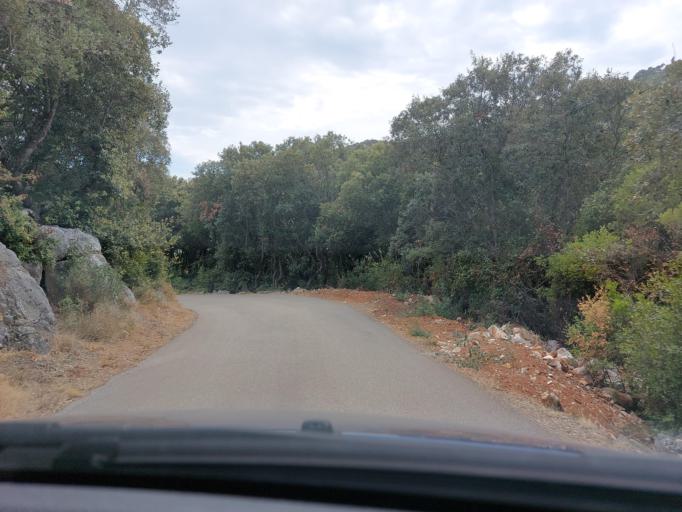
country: HR
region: Dubrovacko-Neretvanska
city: Smokvica
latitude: 42.7568
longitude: 16.9160
